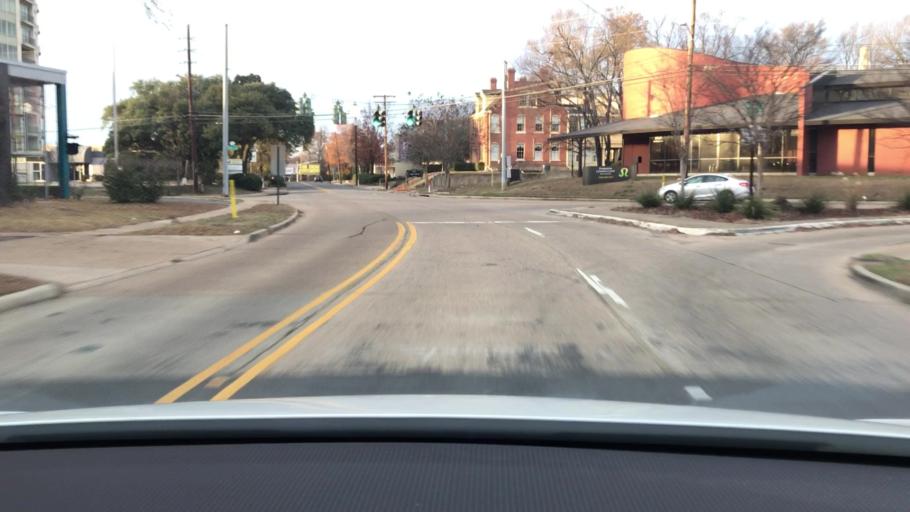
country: US
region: Louisiana
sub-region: Bossier Parish
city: Bossier City
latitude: 32.4924
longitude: -93.7513
